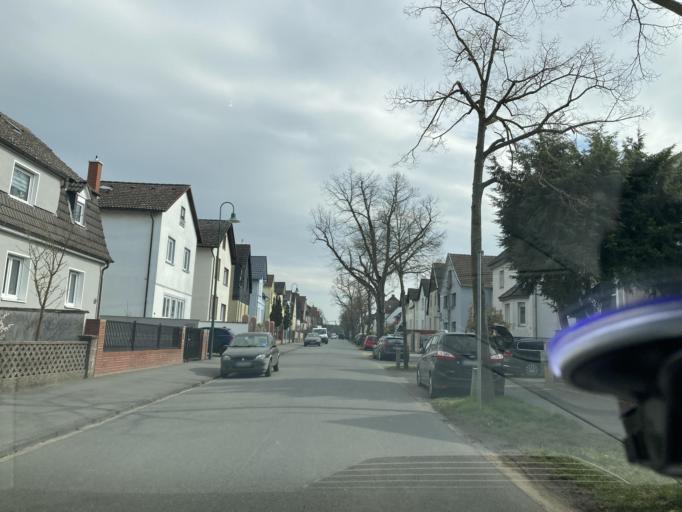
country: DE
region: Hesse
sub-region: Regierungsbezirk Darmstadt
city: Darmstadt
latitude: 49.9116
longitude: 8.6669
